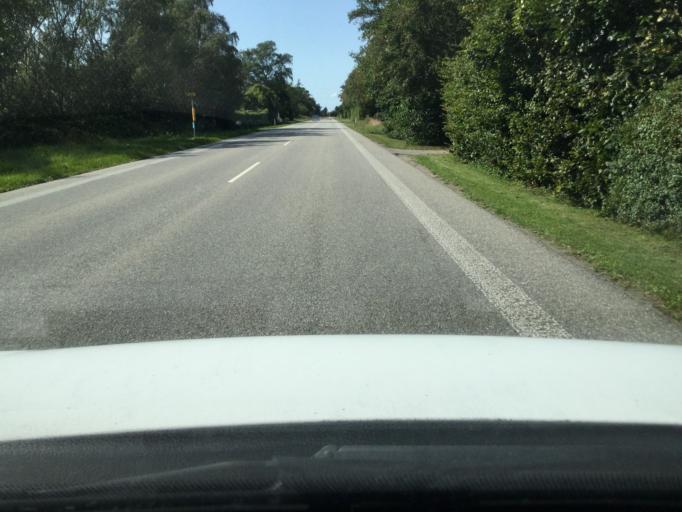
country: DK
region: Zealand
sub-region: Lolland Kommune
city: Rodby
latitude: 54.7621
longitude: 11.3245
